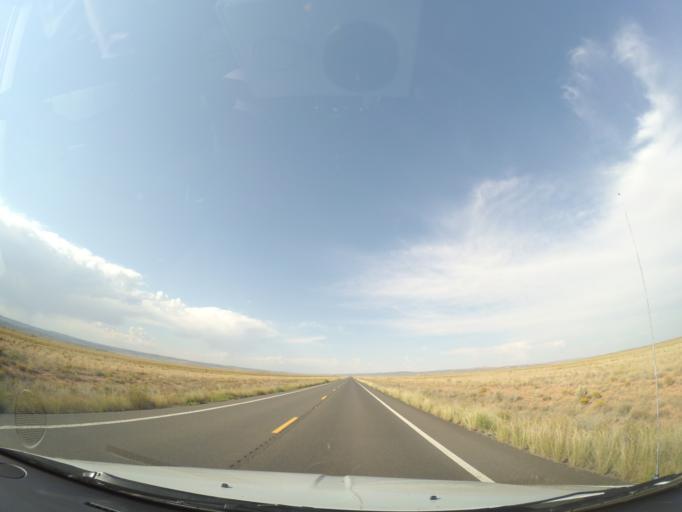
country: US
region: Arizona
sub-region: Coconino County
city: Tuba City
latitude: 36.3695
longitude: -111.4218
